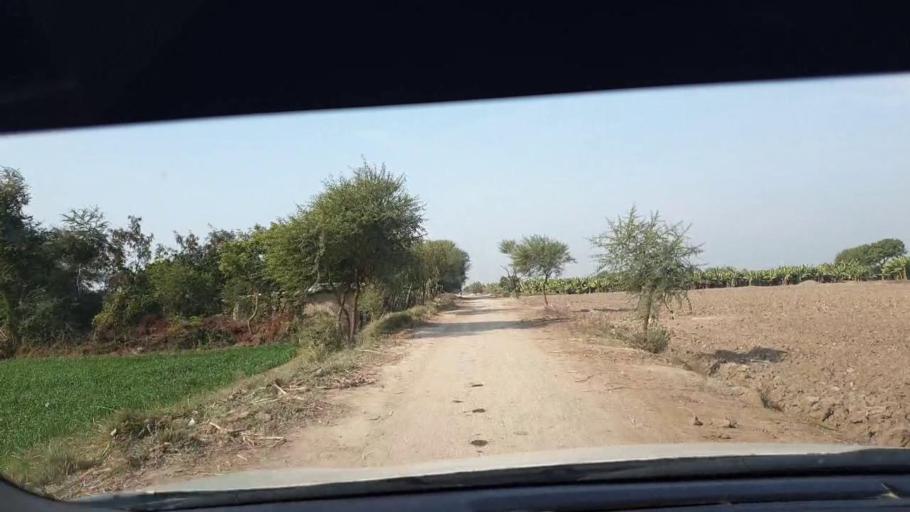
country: PK
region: Sindh
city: Tando Adam
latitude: 25.7650
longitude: 68.7240
